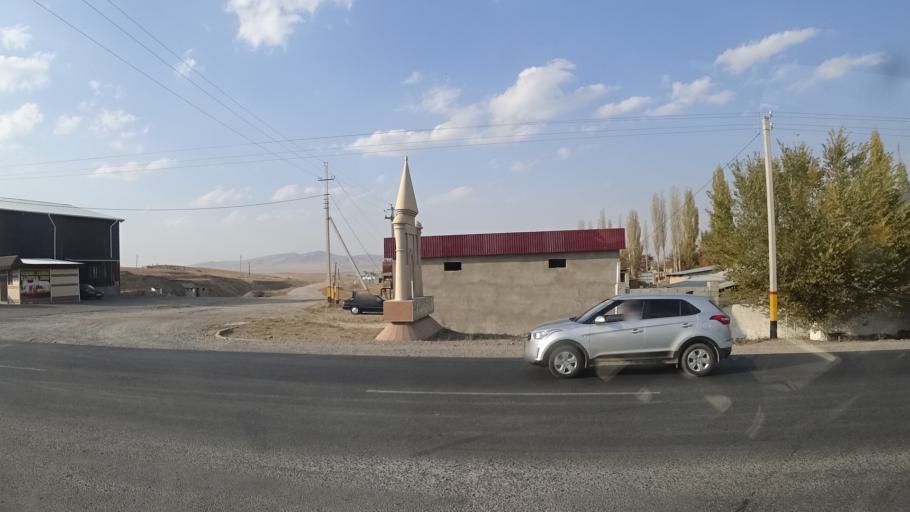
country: KZ
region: Zhambyl
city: Taraz
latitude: 42.8367
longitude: 71.2093
